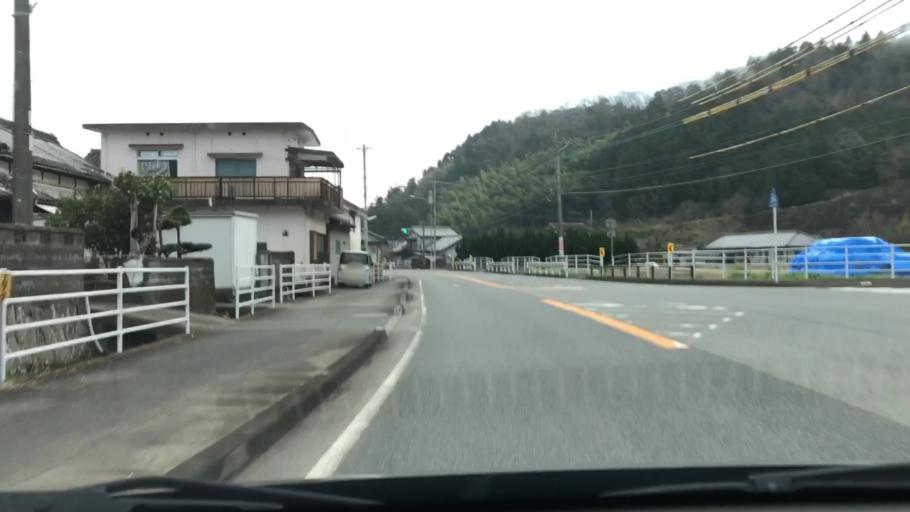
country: JP
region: Oita
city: Saiki
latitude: 32.9862
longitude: 131.8398
